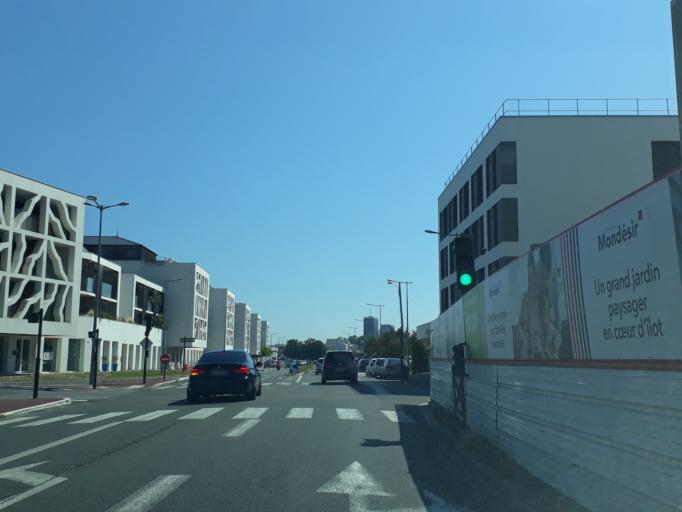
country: FR
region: Aquitaine
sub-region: Departement de la Gironde
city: Merignac
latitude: 44.8369
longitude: -0.6209
